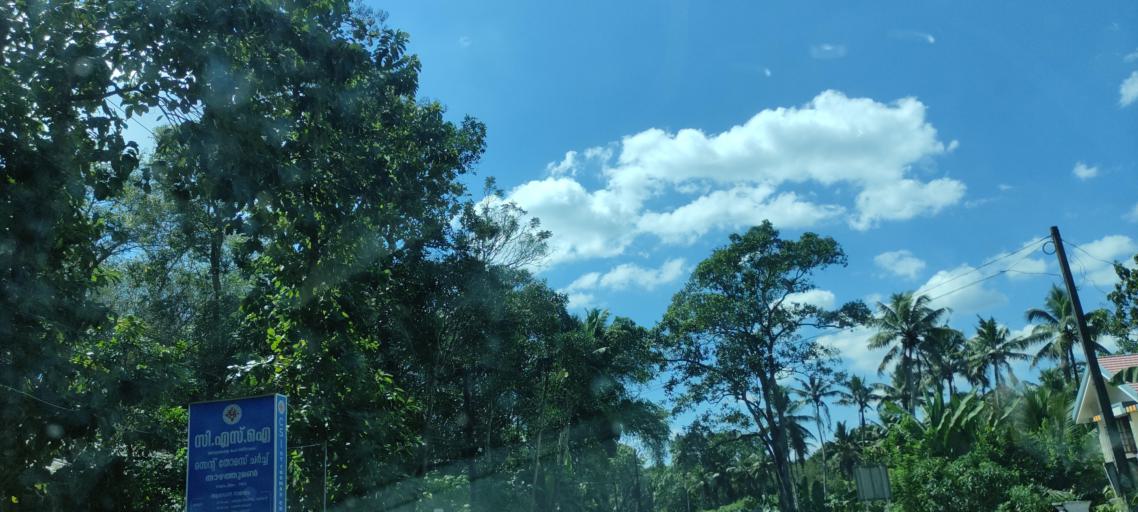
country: IN
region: Kerala
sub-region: Pattanamtitta
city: Adur
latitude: 9.1285
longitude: 76.7075
